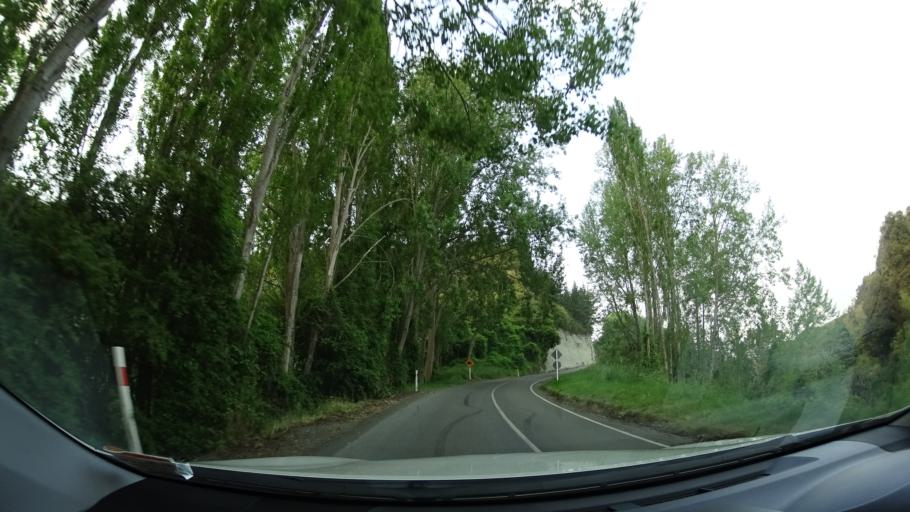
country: NZ
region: Manawatu-Wanganui
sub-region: Ruapehu District
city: Waiouru
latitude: -39.7536
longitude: 175.8356
